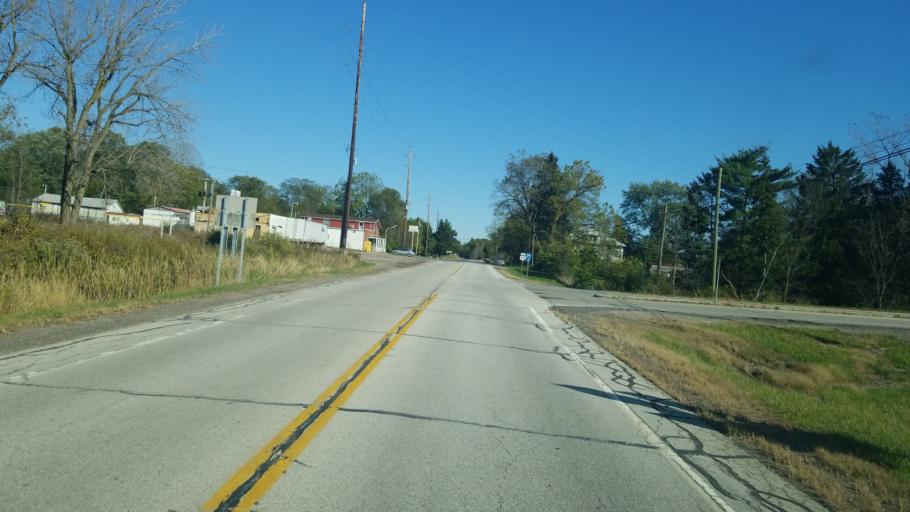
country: US
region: Ohio
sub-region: Medina County
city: Lodi
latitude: 41.0266
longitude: -82.0506
